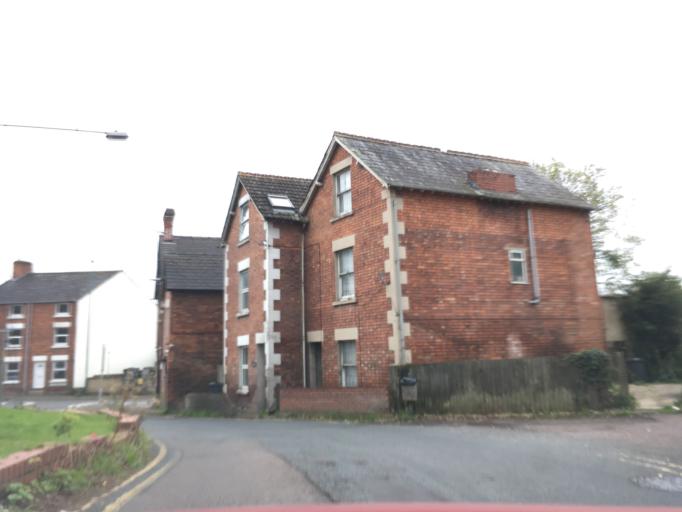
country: GB
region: England
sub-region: Gloucestershire
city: Stonehouse
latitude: 51.7417
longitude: -2.2537
